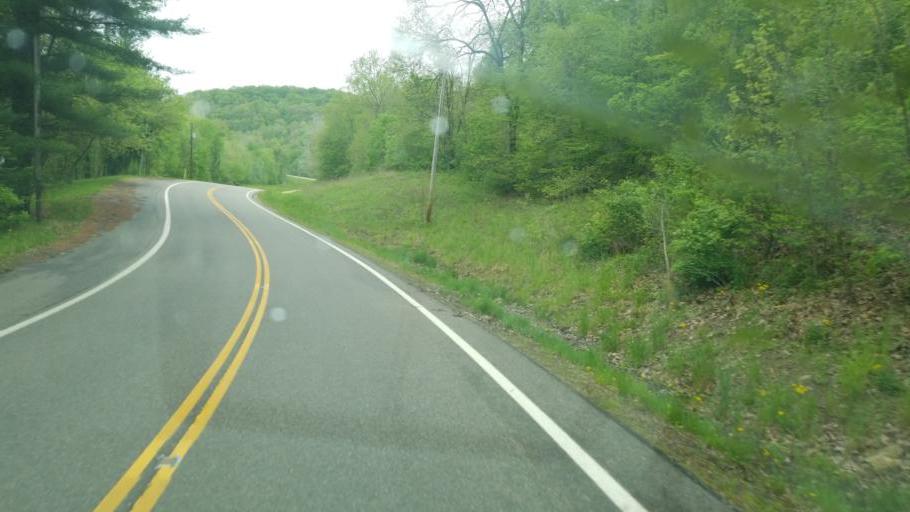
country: US
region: Ohio
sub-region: Guernsey County
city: Mantua
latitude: 40.1604
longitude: -81.6413
